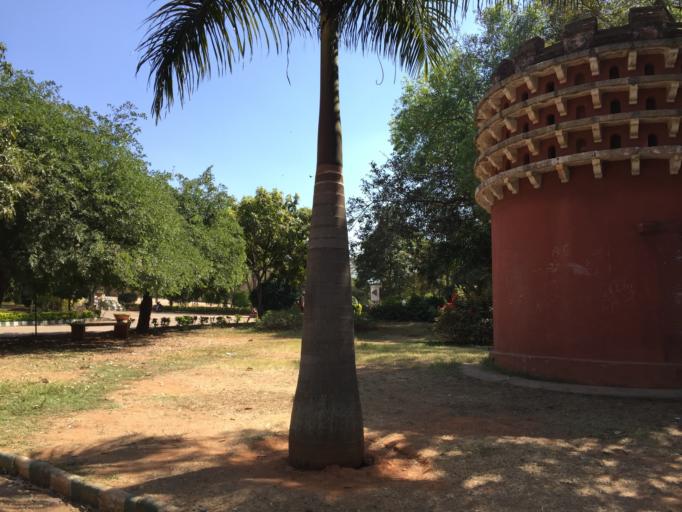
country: IN
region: Karnataka
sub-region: Bangalore Urban
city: Bangalore
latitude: 12.9482
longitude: 77.5880
